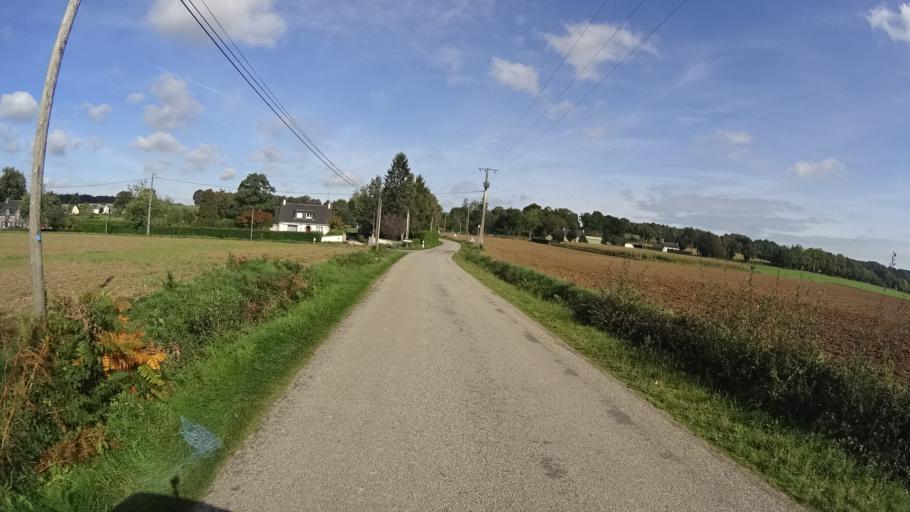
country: FR
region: Brittany
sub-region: Departement du Morbihan
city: Peillac
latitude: 47.7534
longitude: -2.2063
